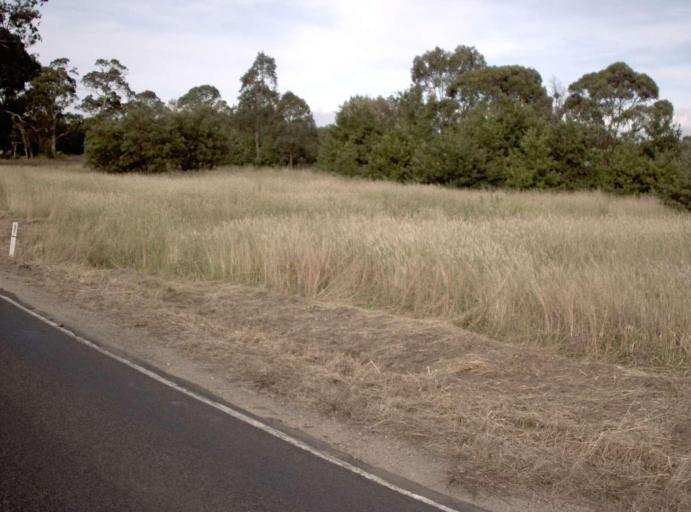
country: AU
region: Victoria
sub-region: Wellington
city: Heyfield
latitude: -37.9889
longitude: 146.7768
